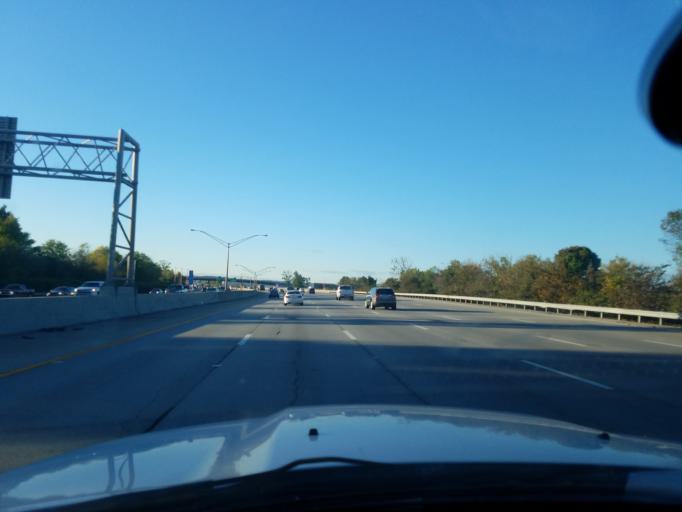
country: US
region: Kentucky
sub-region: Jefferson County
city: Audubon Park
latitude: 38.1742
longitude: -85.7201
